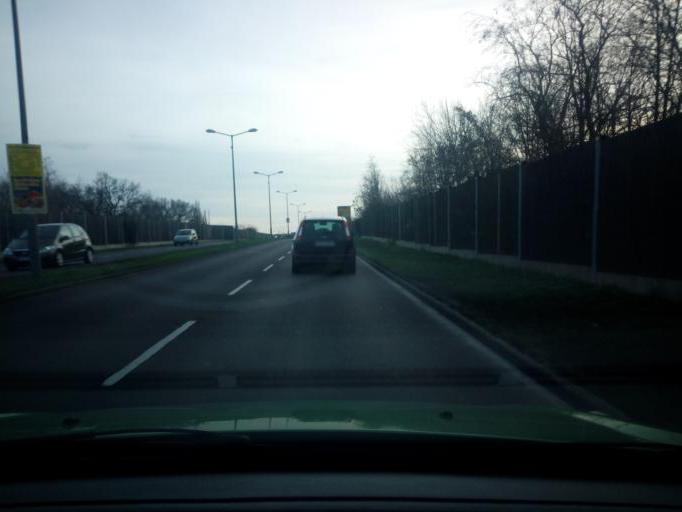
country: DE
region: Berlin
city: Kopenick Bezirk
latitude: 52.4512
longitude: 13.5585
